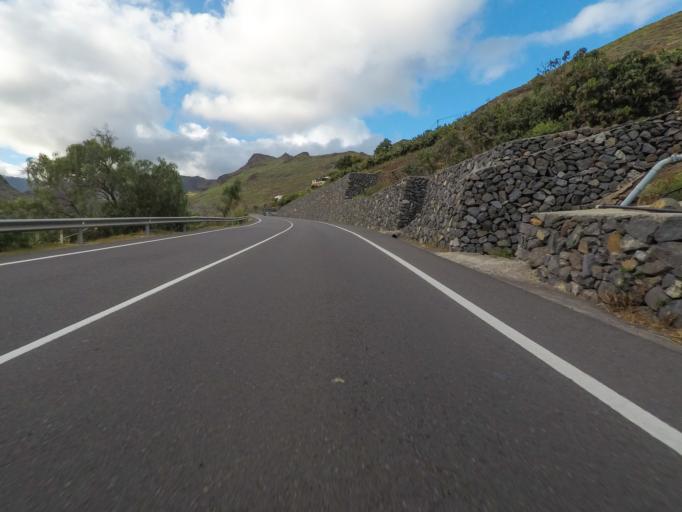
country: ES
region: Canary Islands
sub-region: Provincia de Santa Cruz de Tenerife
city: San Sebastian de la Gomera
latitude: 28.1045
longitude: -17.1235
